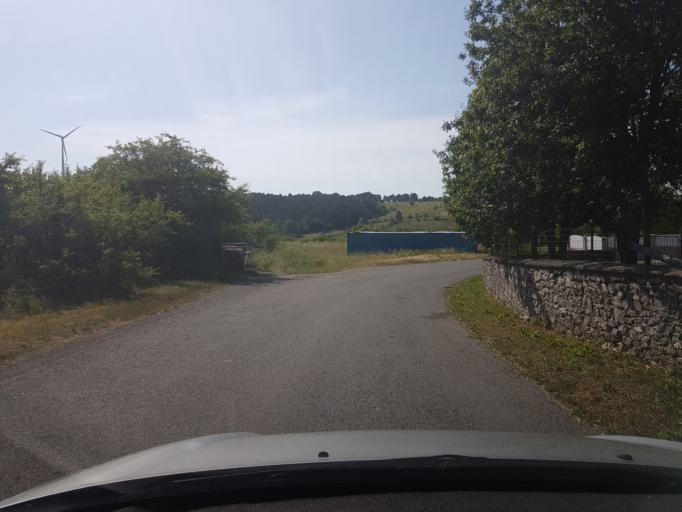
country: SI
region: Divaca
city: Divaca
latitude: 45.7325
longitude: 14.0076
